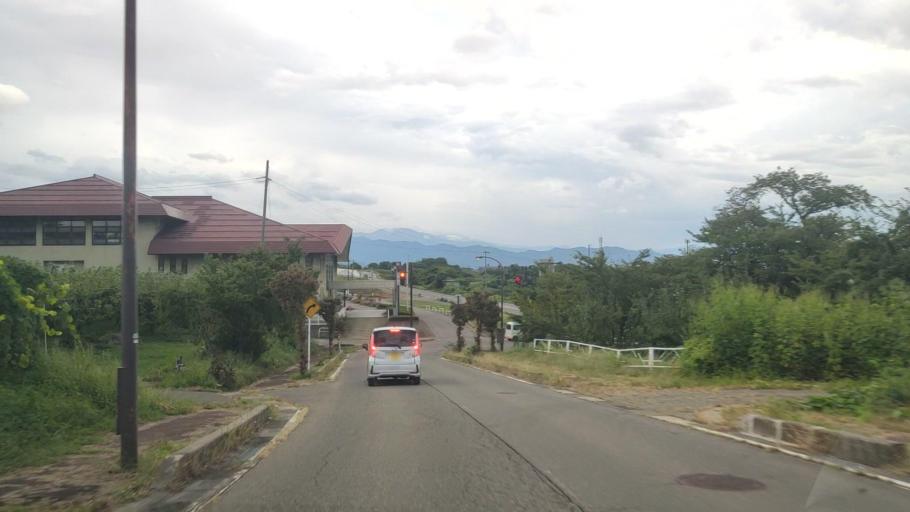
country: JP
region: Nagano
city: Nakano
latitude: 36.7869
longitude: 138.3618
